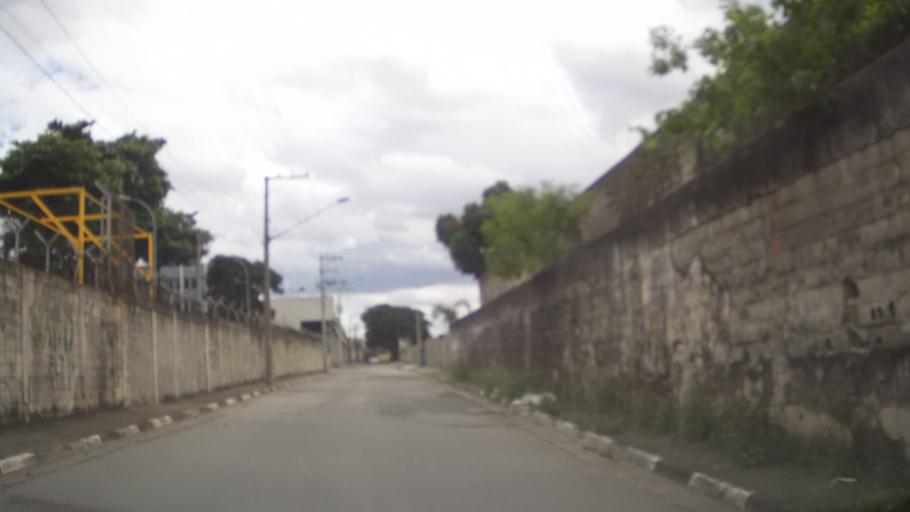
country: BR
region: Sao Paulo
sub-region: Guarulhos
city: Guarulhos
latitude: -23.4918
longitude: -46.5572
